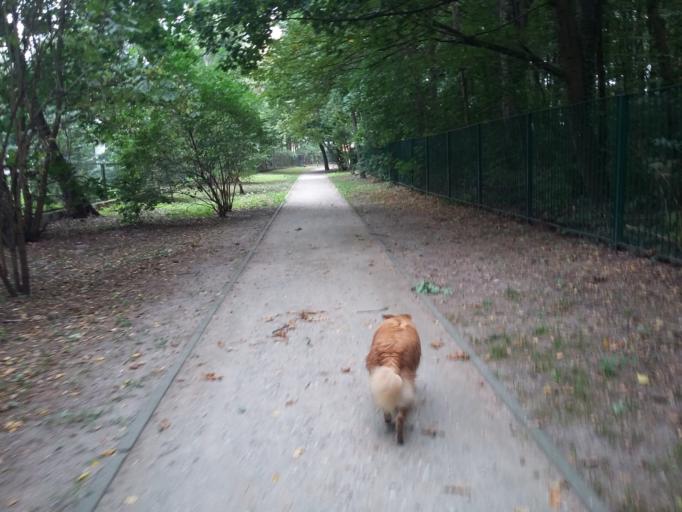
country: PL
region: Lodz Voivodeship
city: Lodz
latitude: 51.7577
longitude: 19.4206
